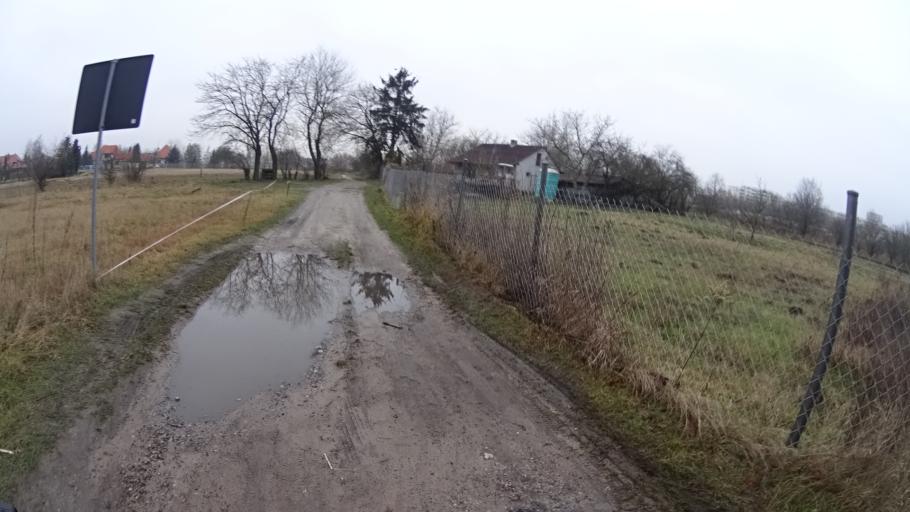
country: PL
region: Masovian Voivodeship
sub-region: Warszawa
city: Ursynow
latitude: 52.1388
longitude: 21.0321
